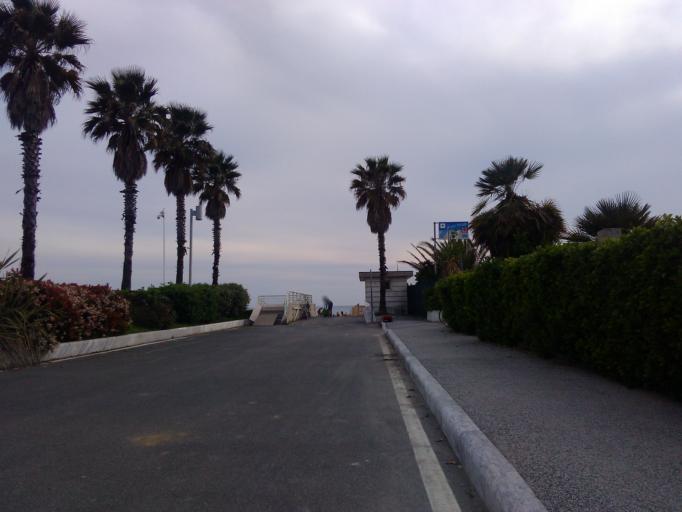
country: IT
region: Tuscany
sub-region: Provincia di Massa-Carrara
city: Massa
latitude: 44.0026
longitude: 10.1071
